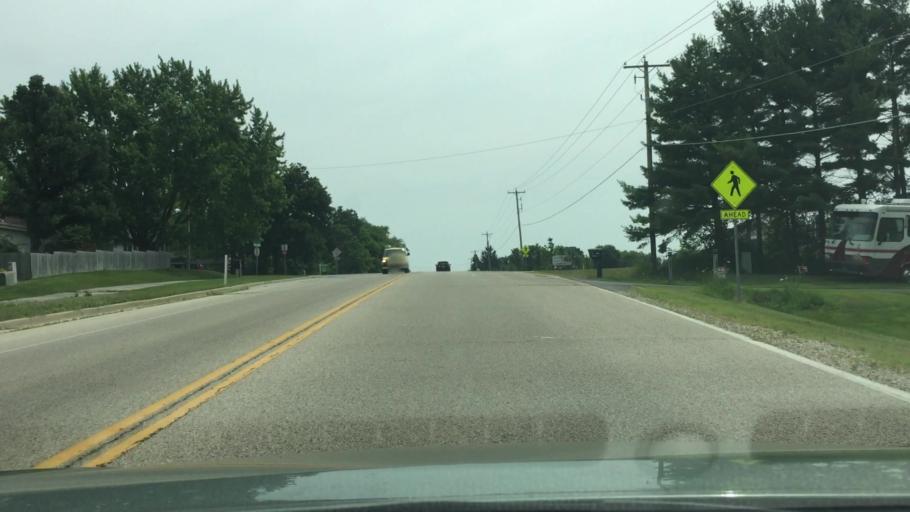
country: US
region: Wisconsin
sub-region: Waukesha County
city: Hartland
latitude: 43.0829
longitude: -88.3410
